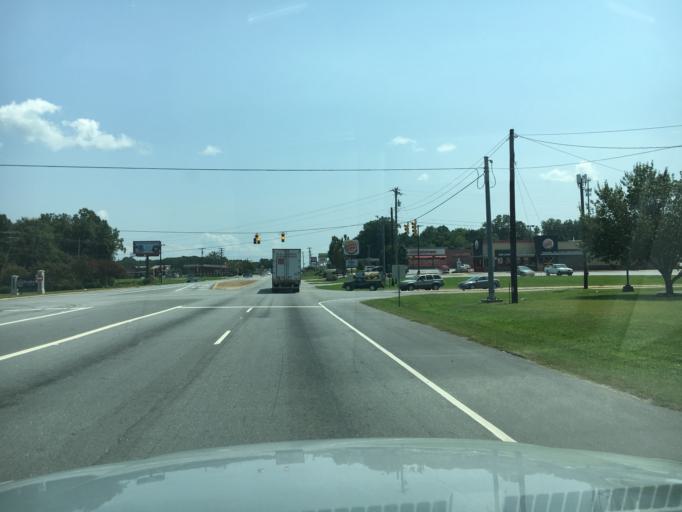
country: US
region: South Carolina
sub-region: Anderson County
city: Pendleton
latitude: 34.6346
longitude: -82.7845
